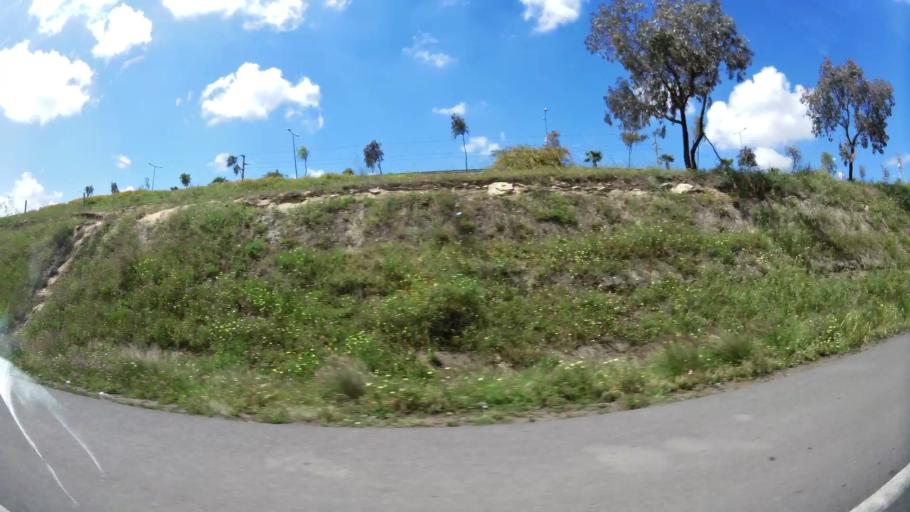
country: MA
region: Grand Casablanca
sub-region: Nouaceur
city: Bouskoura
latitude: 33.4905
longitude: -7.6305
